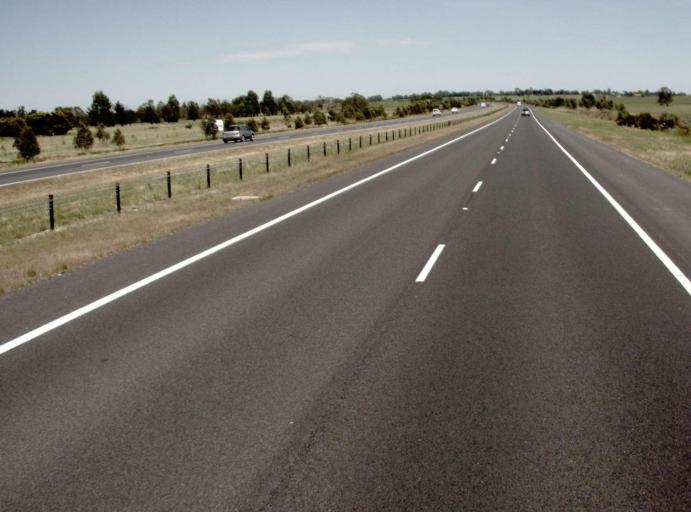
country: AU
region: Victoria
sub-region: Cardinia
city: Pakenham Upper
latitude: -38.0738
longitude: 145.5447
